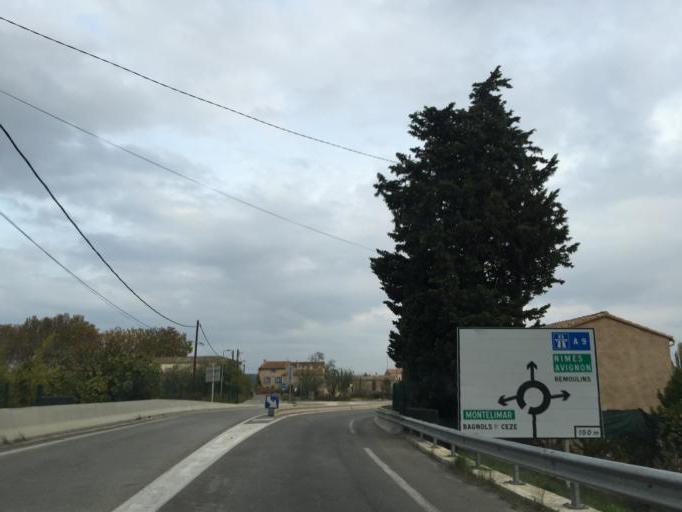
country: FR
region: Languedoc-Roussillon
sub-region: Departement du Gard
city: Castillon-du-Gard
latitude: 43.9553
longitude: 4.5650
